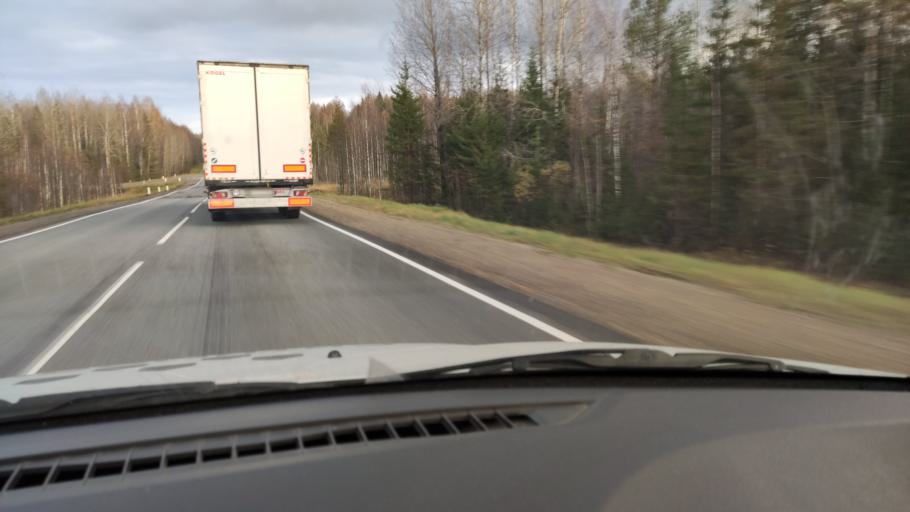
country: RU
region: Kirov
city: Chernaya Kholunitsa
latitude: 58.7733
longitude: 51.9420
